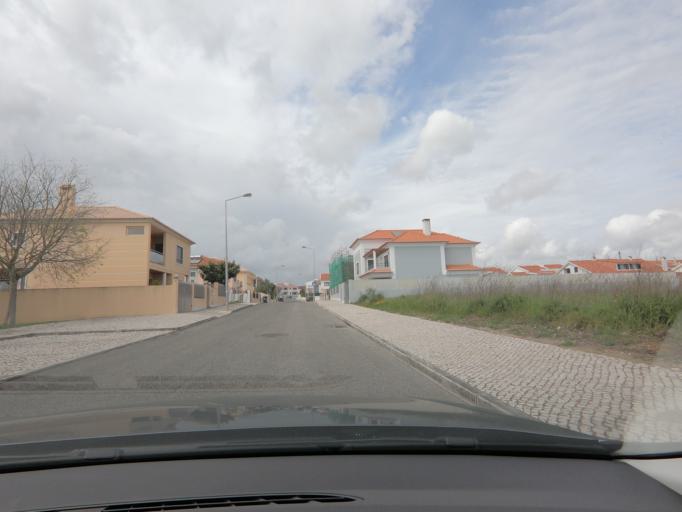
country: PT
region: Lisbon
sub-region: Cascais
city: Sao Domingos de Rana
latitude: 38.7287
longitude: -9.3296
